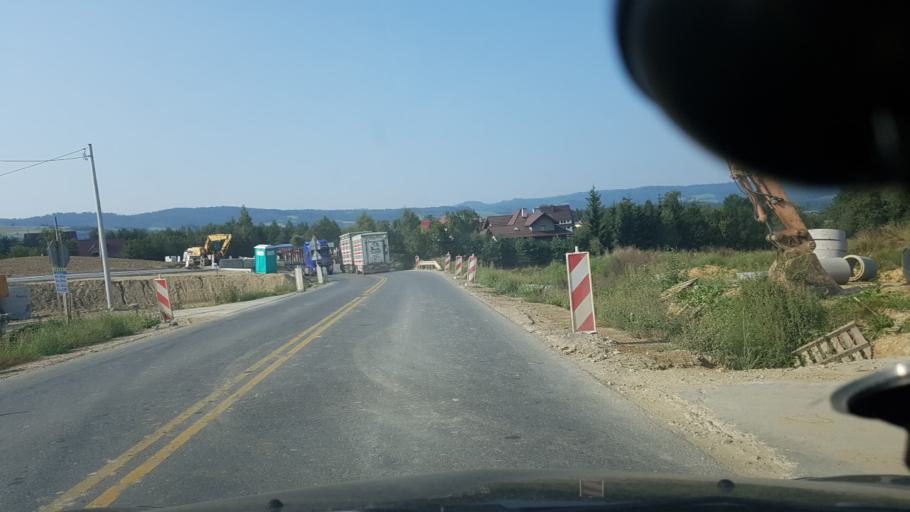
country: PL
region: Lesser Poland Voivodeship
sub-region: Powiat nowotarski
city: Rokiciny
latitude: 49.6042
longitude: 19.9242
